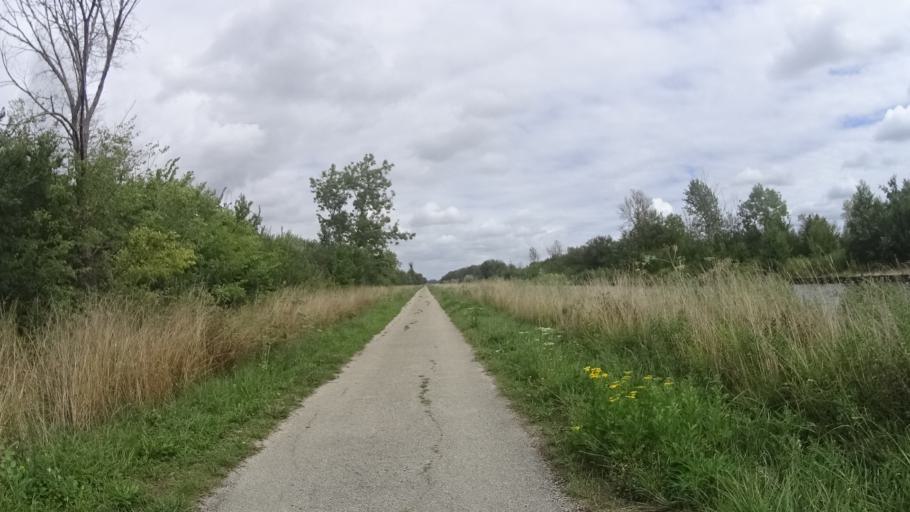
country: FR
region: Picardie
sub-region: Departement de l'Aisne
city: Ognes
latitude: 49.5955
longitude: 3.1958
